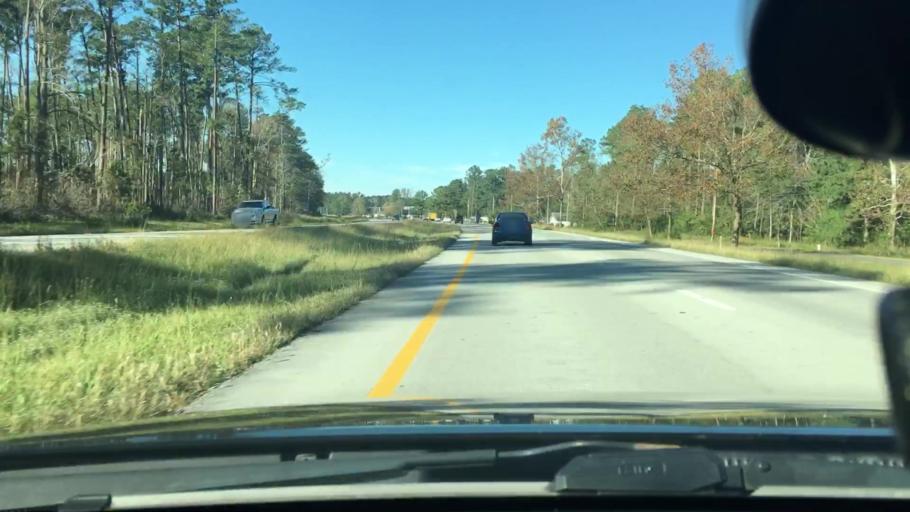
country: US
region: North Carolina
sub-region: Craven County
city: Neuse Forest
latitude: 34.9453
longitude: -76.9484
